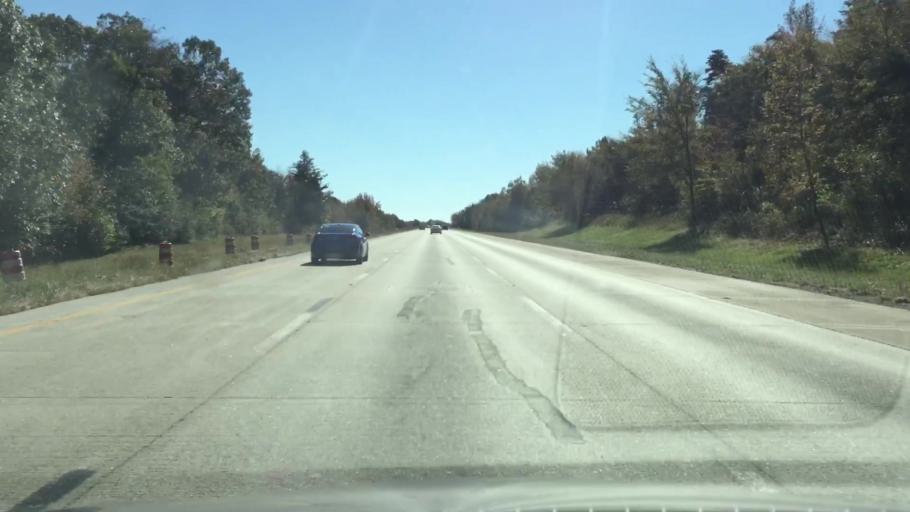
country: US
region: North Carolina
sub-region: Guilford County
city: Jamestown
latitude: 35.9700
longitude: -79.8923
